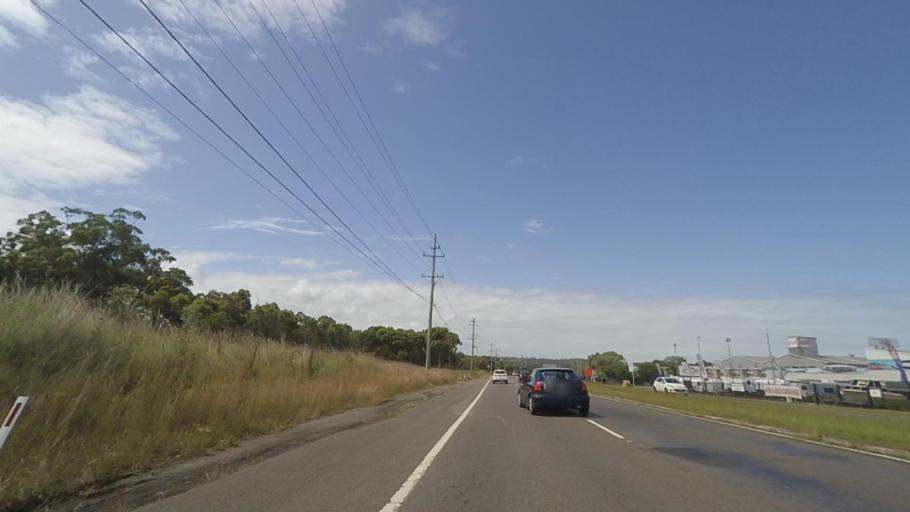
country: AU
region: New South Wales
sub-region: Lake Macquarie Shire
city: Windale
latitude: -32.9969
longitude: 151.6864
